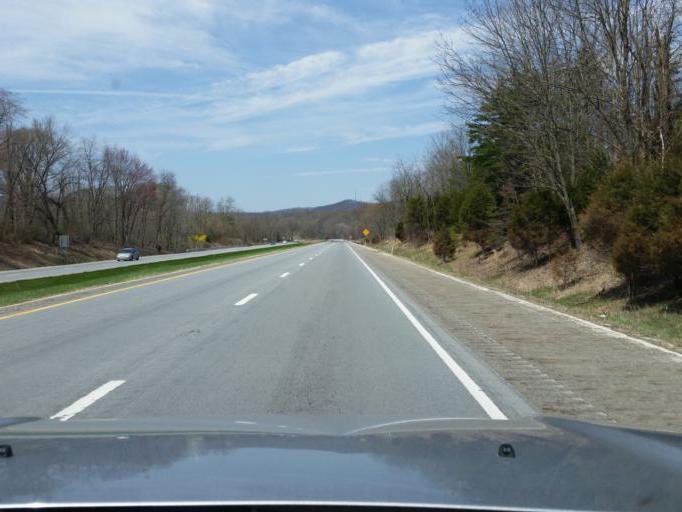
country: US
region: Pennsylvania
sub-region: Perry County
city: Newport
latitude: 40.5350
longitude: -77.1407
